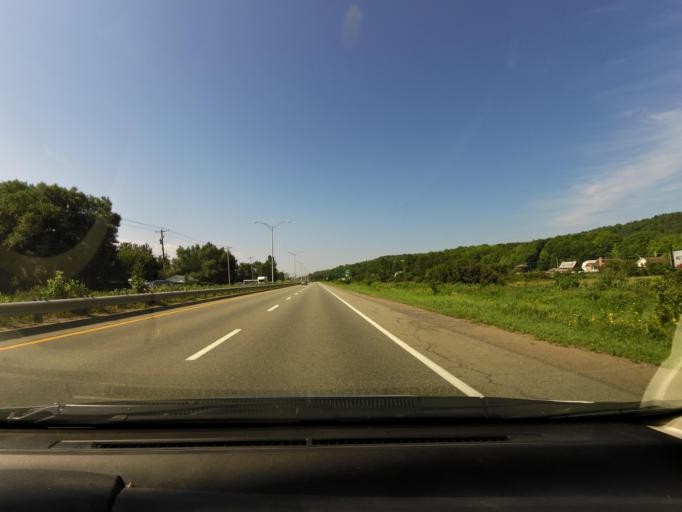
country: CA
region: Quebec
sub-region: Capitale-Nationale
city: Chateau-Richer
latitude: 46.9838
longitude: -70.9999
